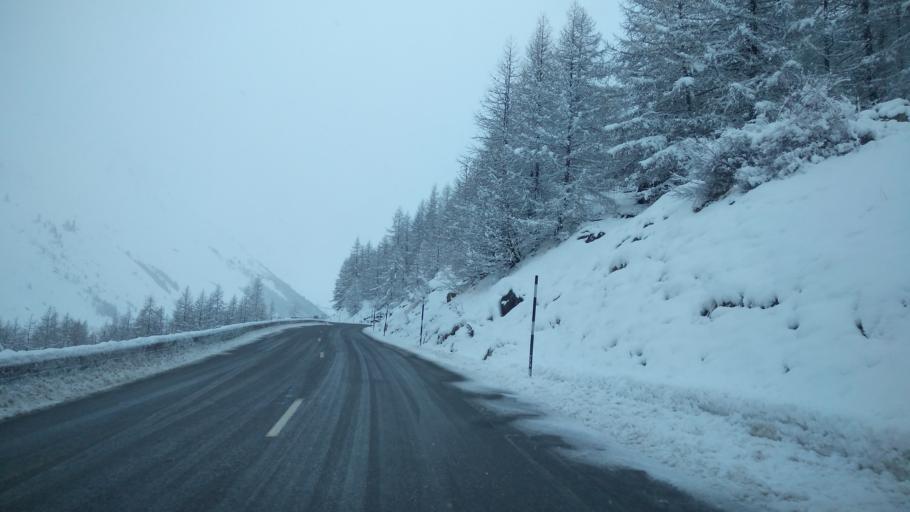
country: FR
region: Provence-Alpes-Cote d'Azur
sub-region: Departement des Hautes-Alpes
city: Le Monetier-les-Bains
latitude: 45.0243
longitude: 6.4544
